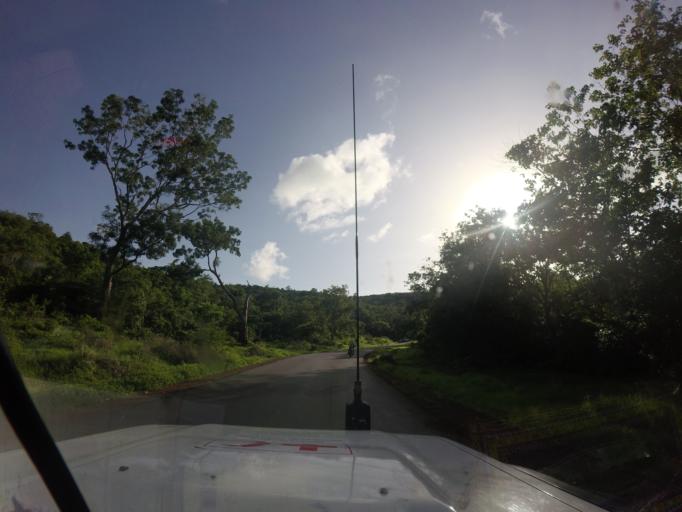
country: GN
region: Kindia
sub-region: Kindia
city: Kindia
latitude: 10.0102
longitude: -12.8053
